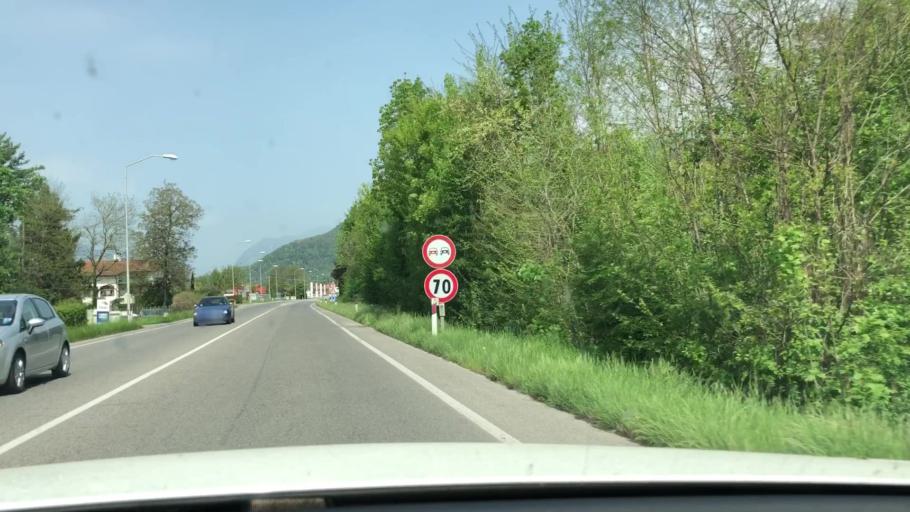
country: IT
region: Friuli Venezia Giulia
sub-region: Provincia di Udine
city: Magnano in Riviera
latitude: 46.2134
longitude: 13.1833
